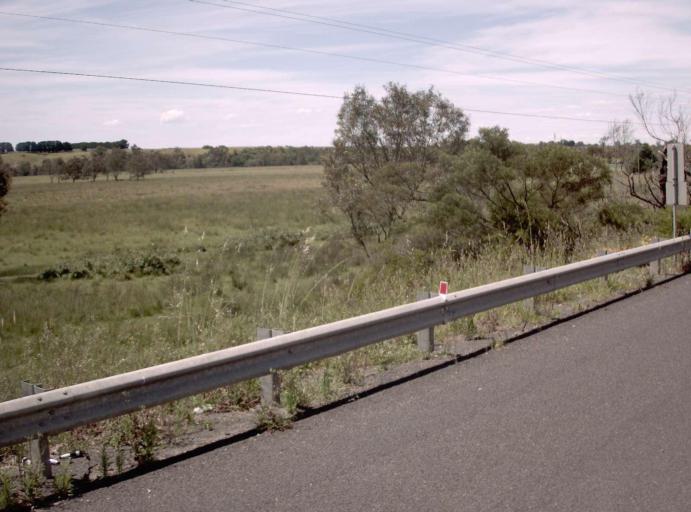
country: AU
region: Victoria
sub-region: Wellington
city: Heyfield
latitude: -38.1508
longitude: 146.7743
